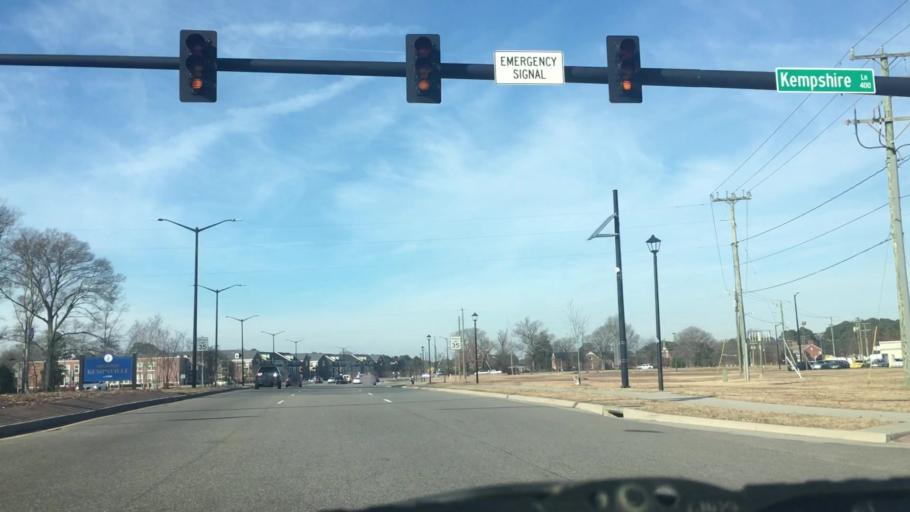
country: US
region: Virginia
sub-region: City of Chesapeake
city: Chesapeake
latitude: 36.8252
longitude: -76.1579
